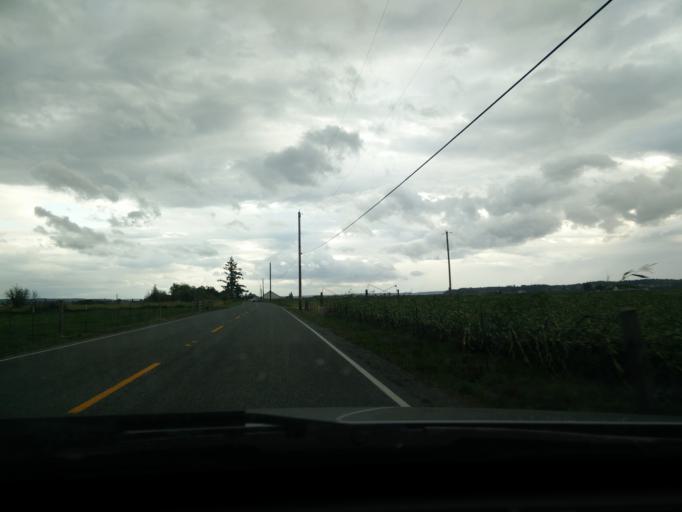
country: US
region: Washington
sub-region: Snohomish County
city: Stanwood
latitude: 48.2662
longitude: -122.3677
